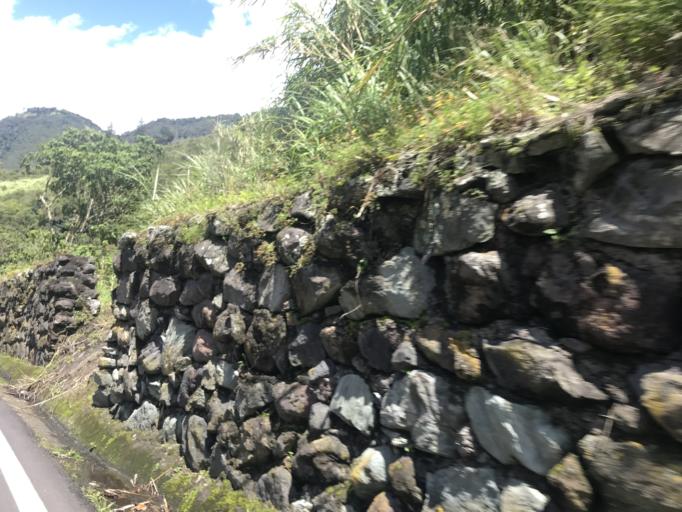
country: EC
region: Tungurahua
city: Banos
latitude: -1.4035
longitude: -78.4058
